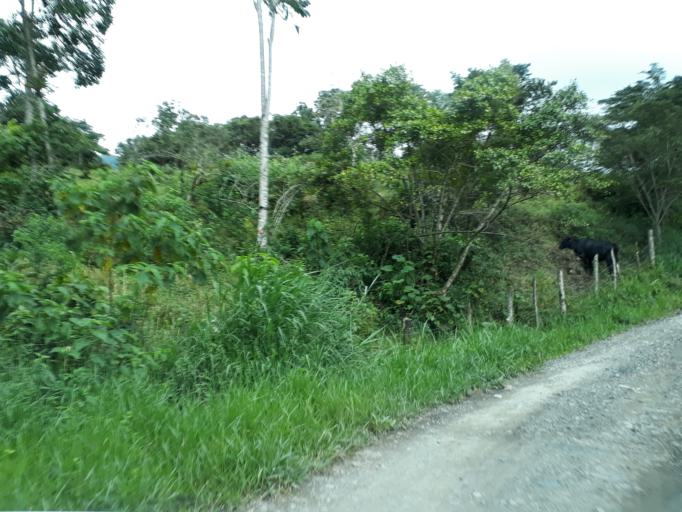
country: CO
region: Boyaca
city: Muzo
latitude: 5.3796
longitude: -74.0910
